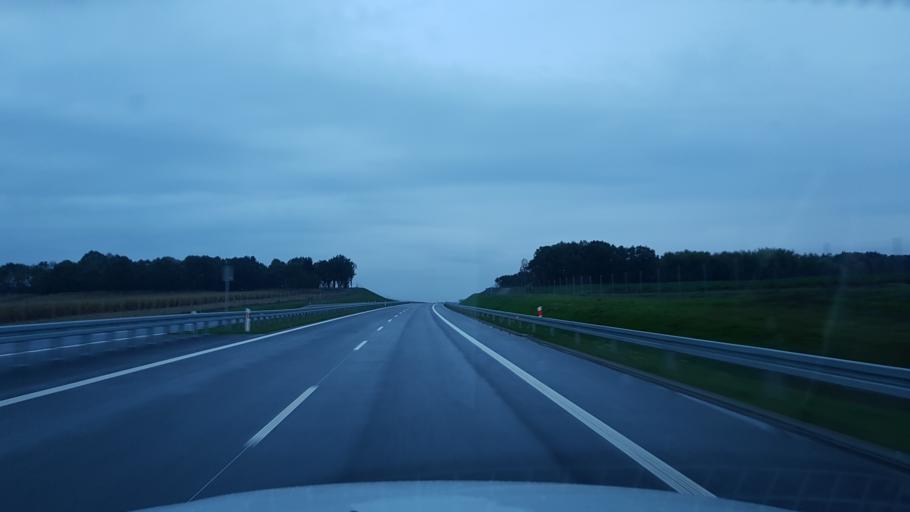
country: PL
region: West Pomeranian Voivodeship
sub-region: Powiat gryficki
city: Brojce
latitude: 53.9098
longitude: 15.3813
